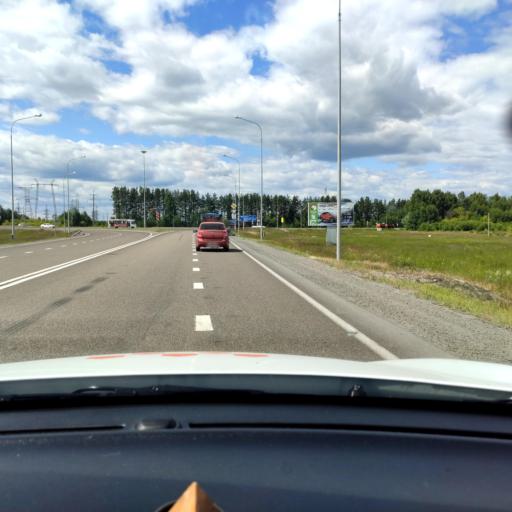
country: RU
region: Mariy-El
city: Volzhsk
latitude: 55.9116
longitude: 48.3689
